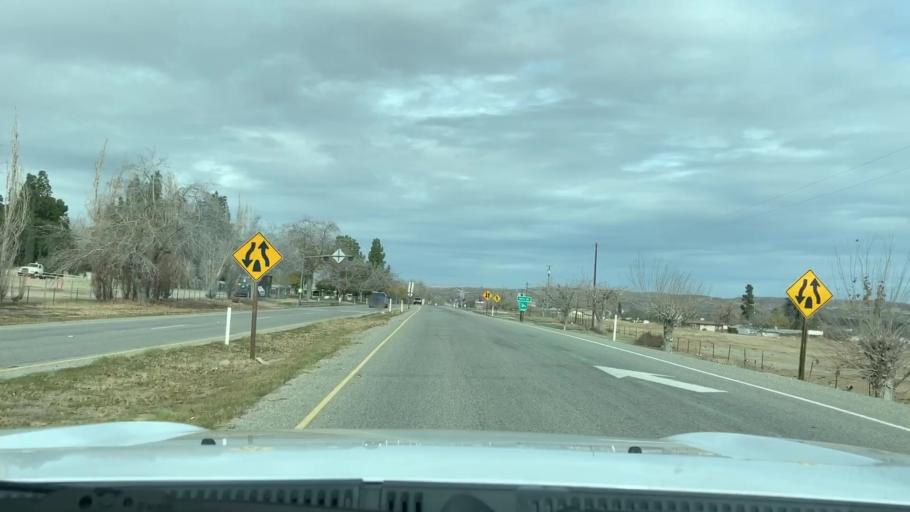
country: US
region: California
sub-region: Kern County
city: South Taft
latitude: 35.1386
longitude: -119.4471
